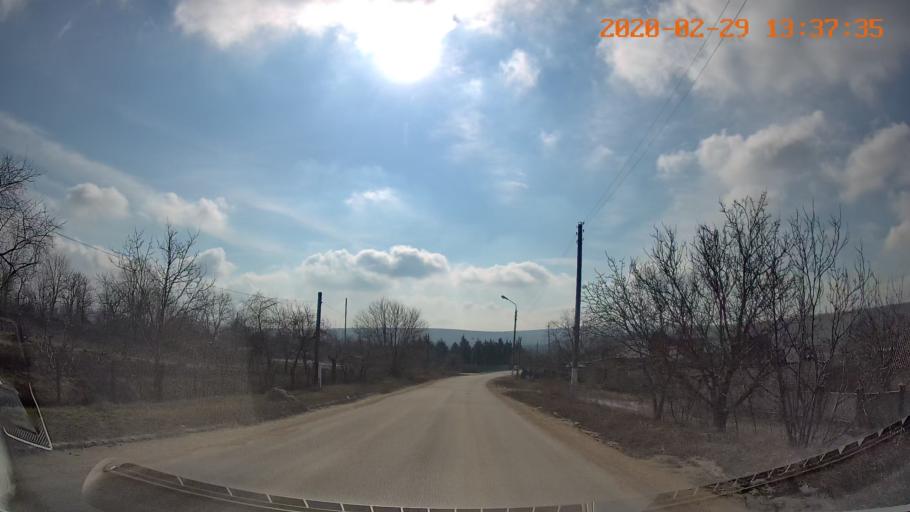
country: MD
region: Telenesti
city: Camenca
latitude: 47.8618
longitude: 28.6017
